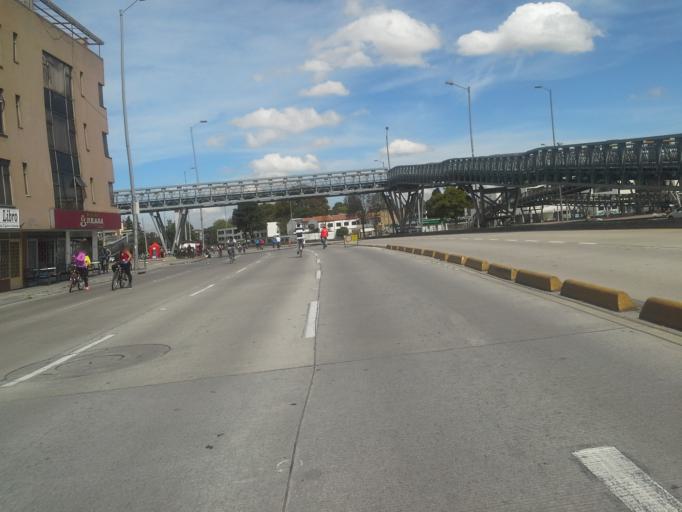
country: CO
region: Bogota D.C.
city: Bogota
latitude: 4.6315
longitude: -74.0840
